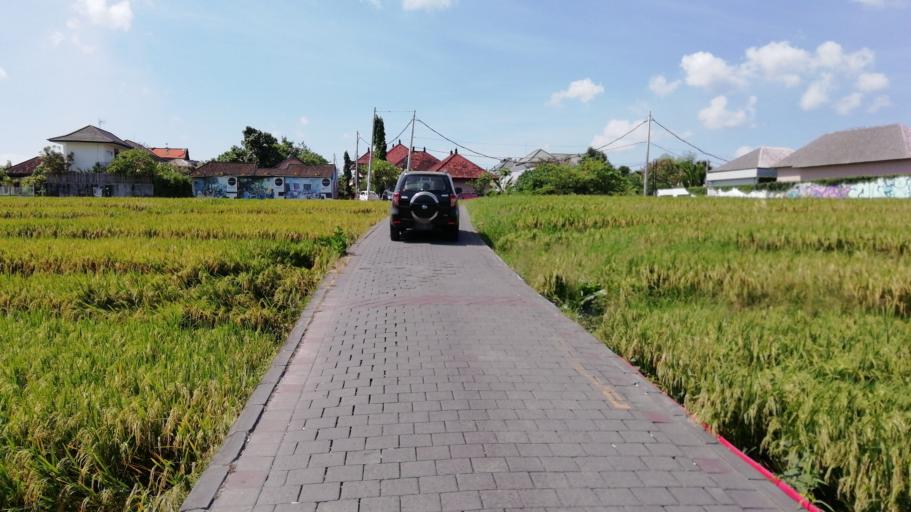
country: ID
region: Bali
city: Banjar Kerobokan
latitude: -8.6540
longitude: 115.1397
